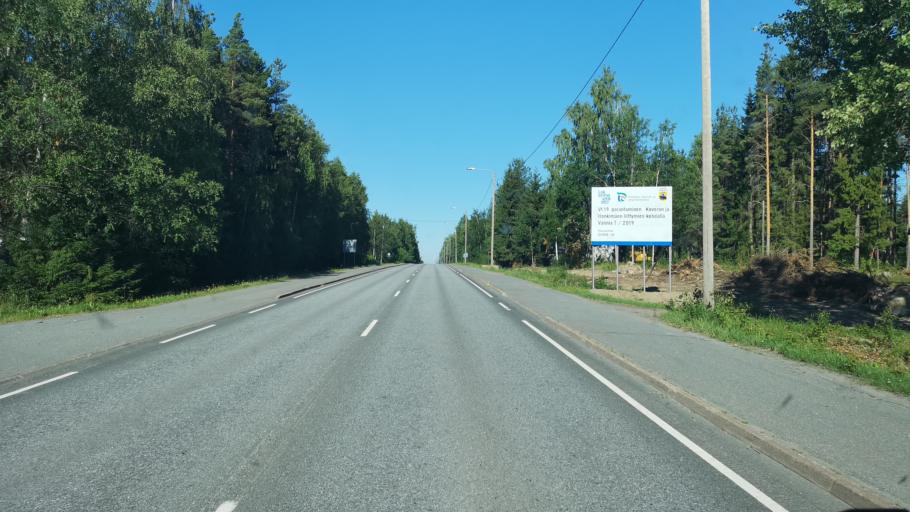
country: FI
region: Southern Ostrobothnia
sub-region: Seinaejoki
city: Lapua
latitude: 62.9697
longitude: 23.0687
